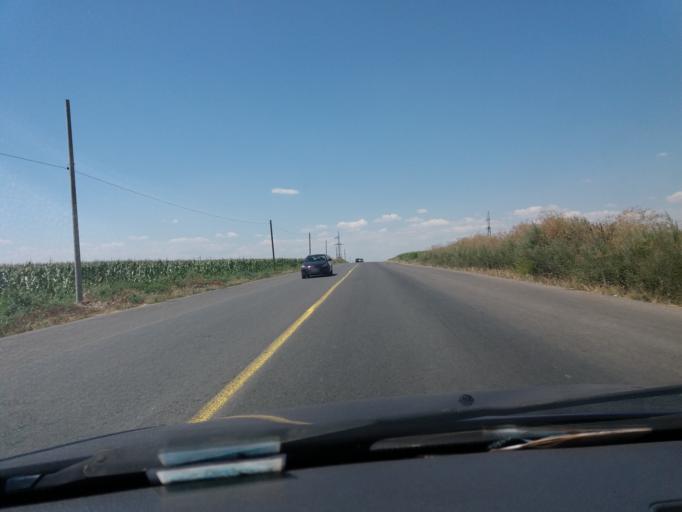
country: RO
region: Constanta
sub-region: Comuna Lumina
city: Lumina
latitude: 44.2857
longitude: 28.5838
